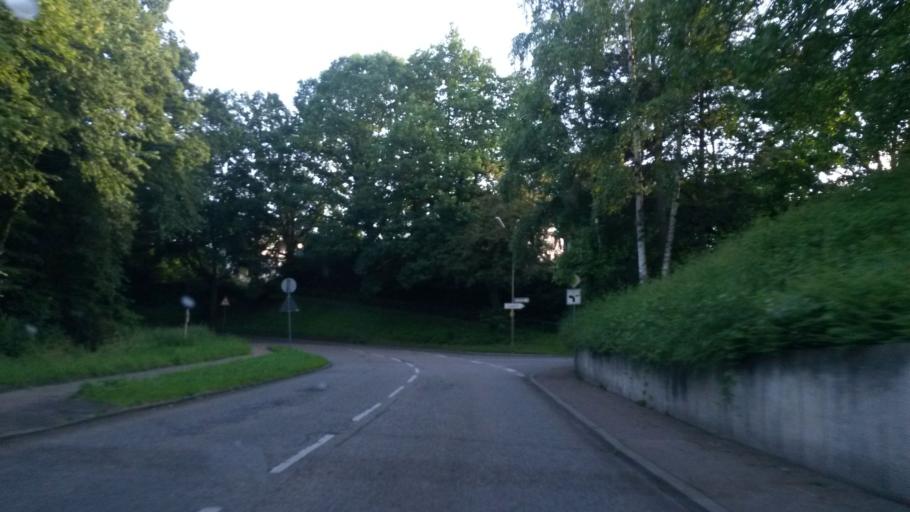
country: DE
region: Baden-Wuerttemberg
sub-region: Karlsruhe Region
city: Pforzheim
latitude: 48.8771
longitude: 8.6738
